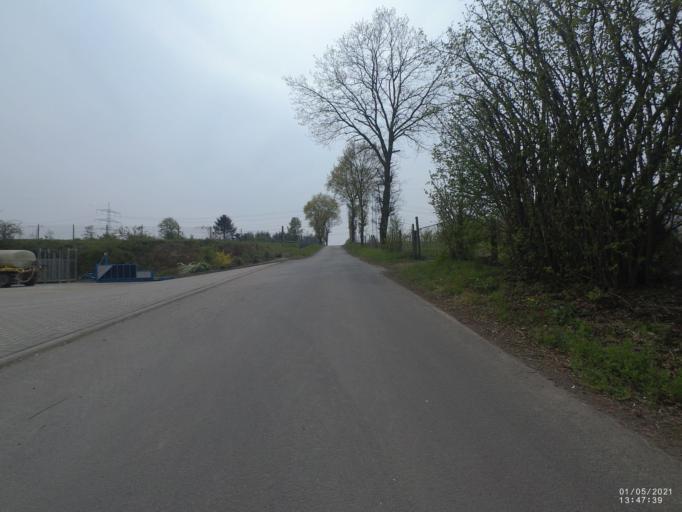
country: DE
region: Rheinland-Pfalz
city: Bassenheim
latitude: 50.3822
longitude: 7.4599
